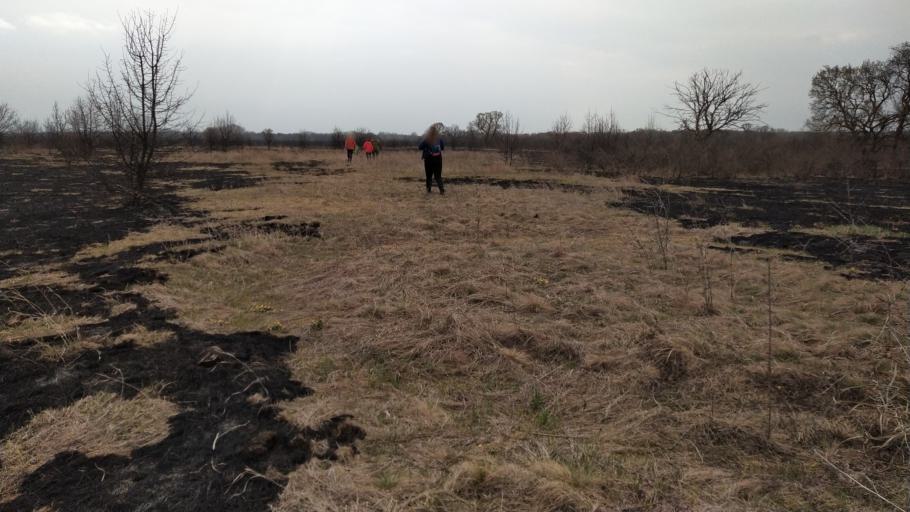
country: RU
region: Rostov
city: Semikarakorsk
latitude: 47.5505
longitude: 40.6772
